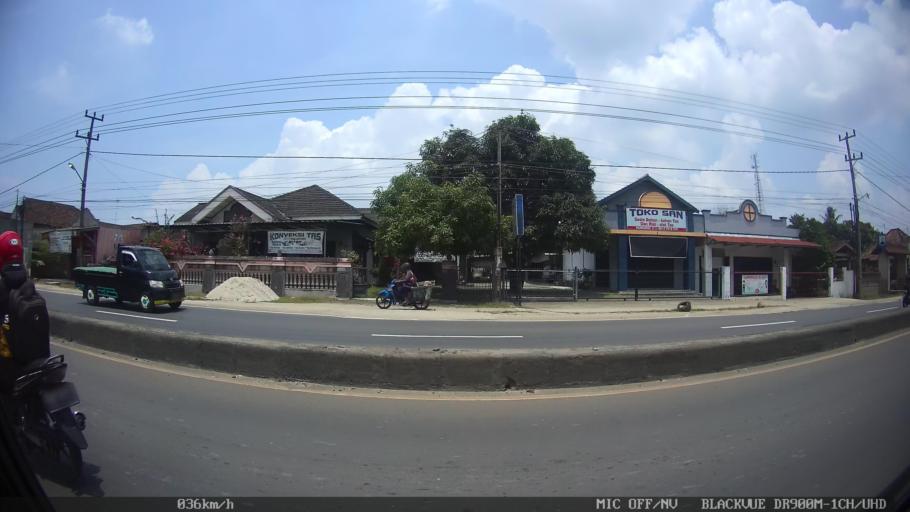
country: ID
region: Lampung
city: Natar
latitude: -5.3261
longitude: 105.2021
